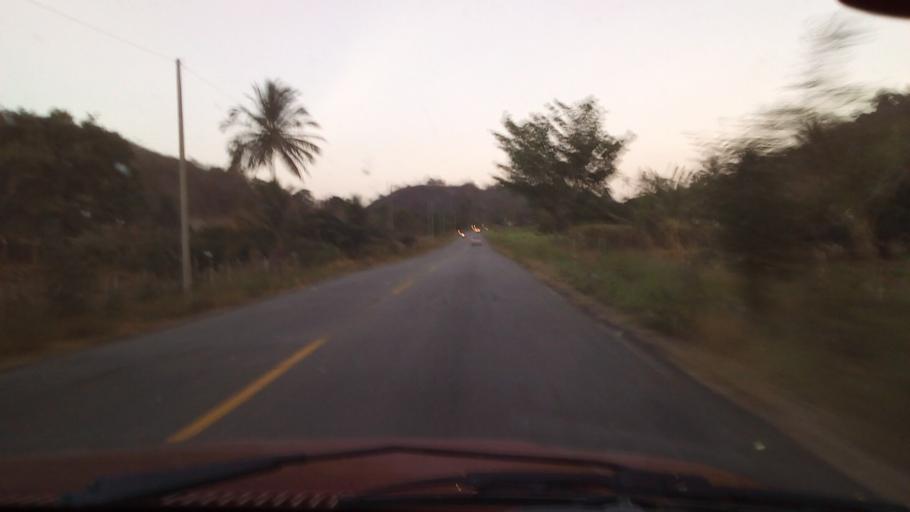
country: BR
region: Paraiba
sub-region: Bananeiras
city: Solanea
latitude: -6.7383
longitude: -35.5357
